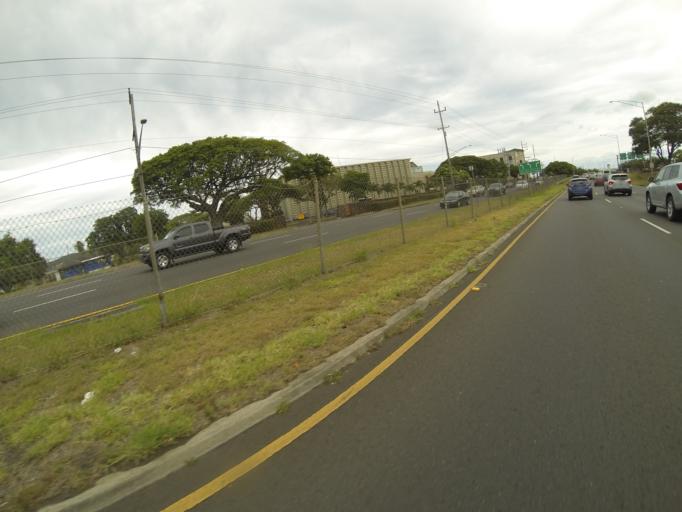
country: US
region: Hawaii
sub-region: Honolulu County
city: Honolulu
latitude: 21.3353
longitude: -157.8706
